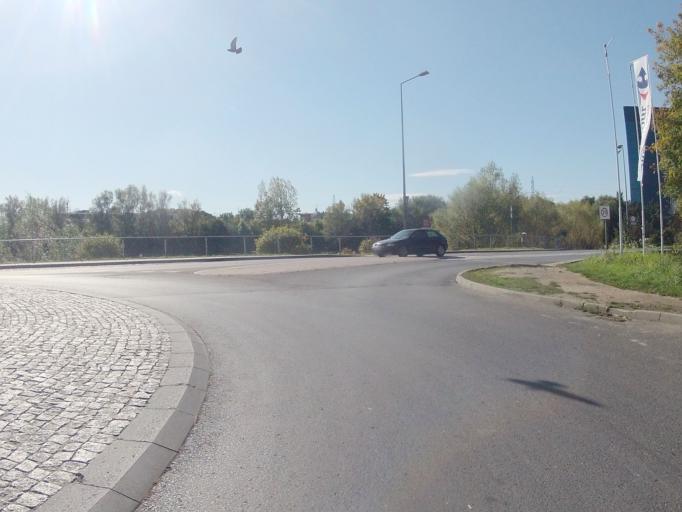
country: PL
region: Lesser Poland Voivodeship
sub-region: Krakow
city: Krakow
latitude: 50.0657
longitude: 19.9861
